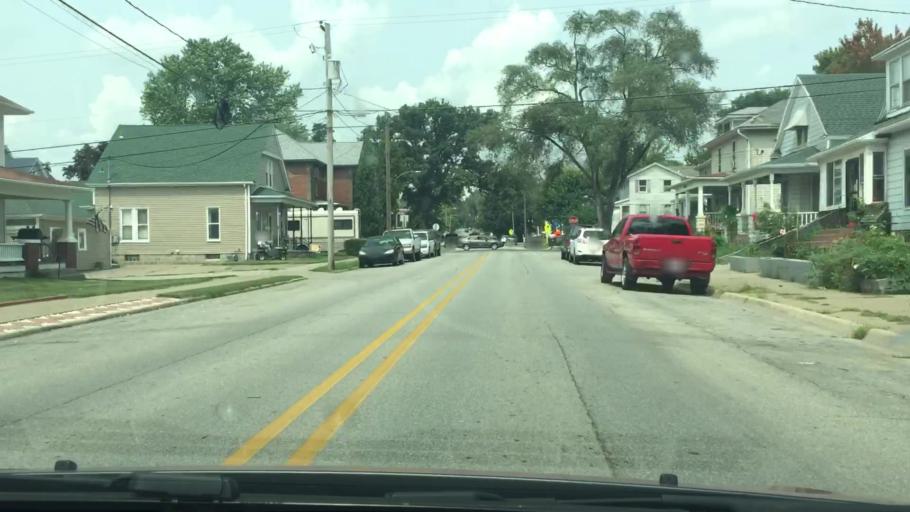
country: US
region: Iowa
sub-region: Muscatine County
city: Muscatine
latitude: 41.4278
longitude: -91.0455
